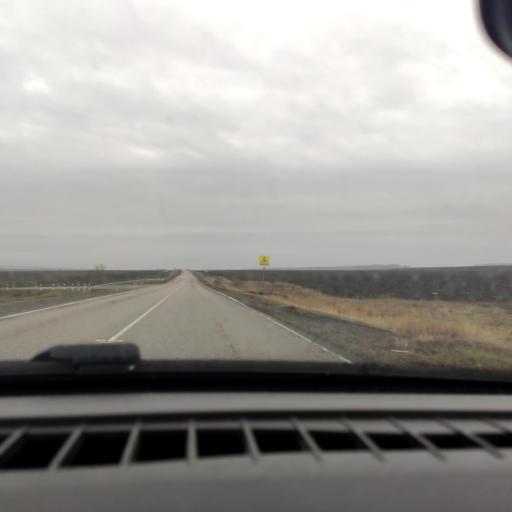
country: RU
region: Belgorod
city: Ilovka
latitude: 50.7777
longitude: 38.8154
